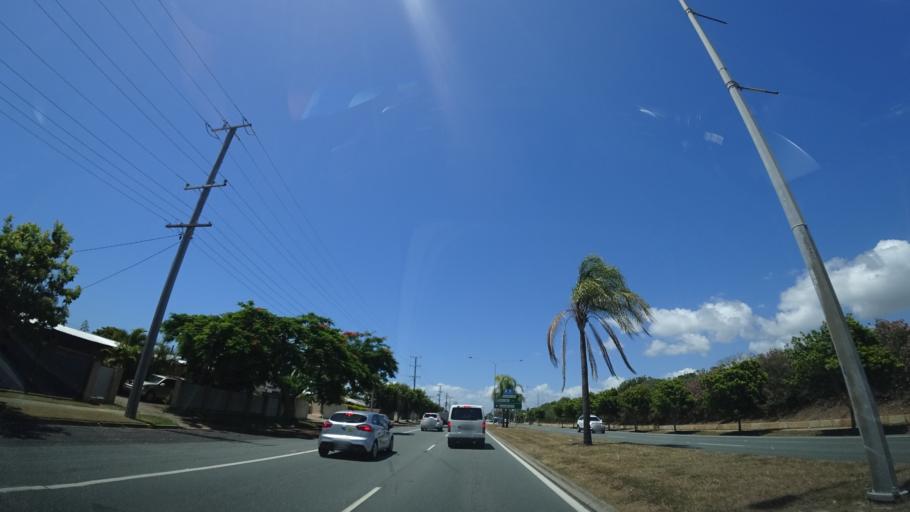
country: AU
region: Queensland
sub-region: Sunshine Coast
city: Mooloolaba
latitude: -26.7173
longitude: 153.1299
